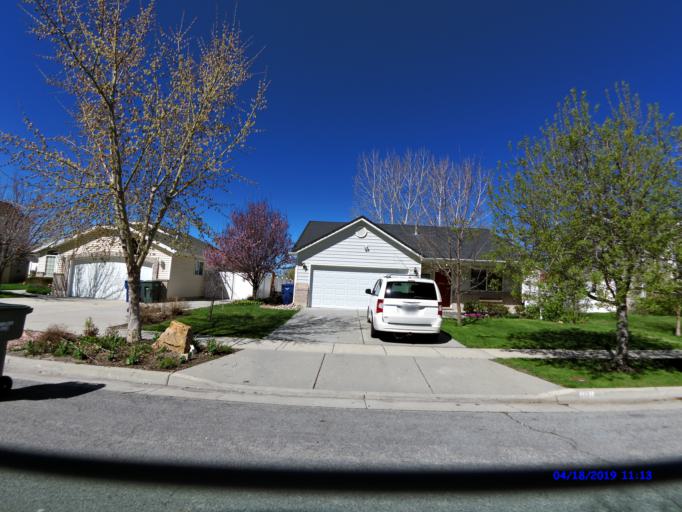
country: US
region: Utah
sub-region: Weber County
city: North Ogden
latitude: 41.2837
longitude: -111.9548
